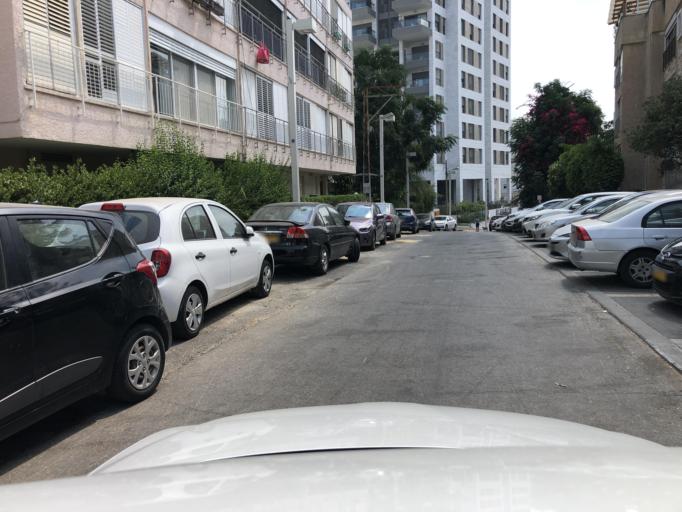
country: IL
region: Tel Aviv
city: Ramat Gan
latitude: 32.0778
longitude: 34.8132
